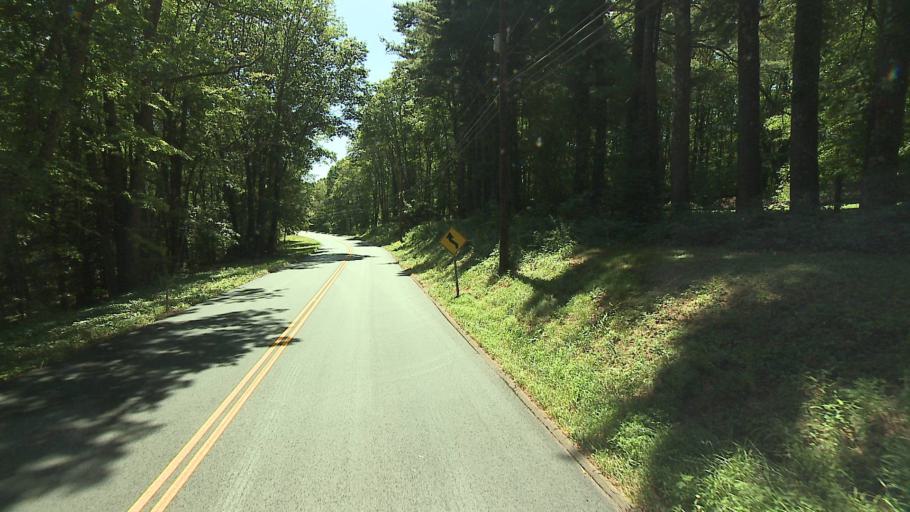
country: US
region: Connecticut
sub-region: Hartford County
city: West Simsbury
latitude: 41.9113
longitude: -72.9005
